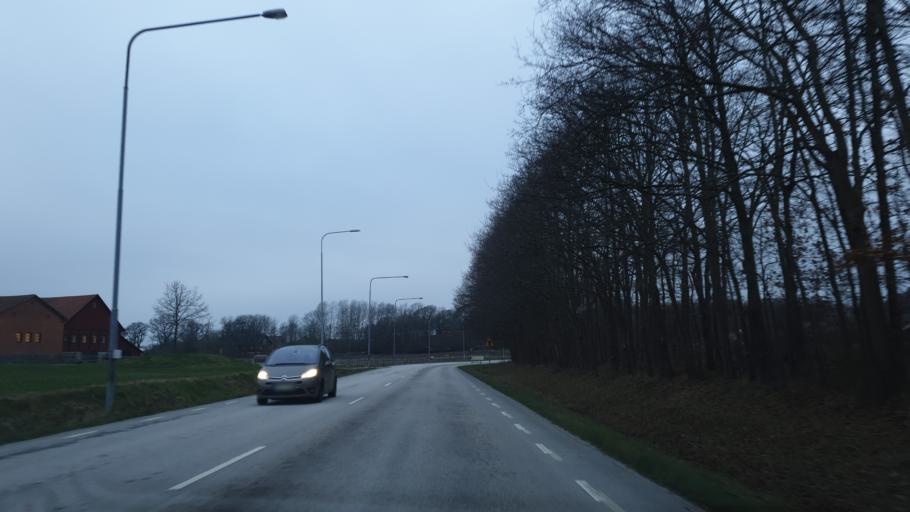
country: SE
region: Blekinge
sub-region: Karlskrona Kommun
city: Rodeby
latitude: 56.2069
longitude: 15.6572
